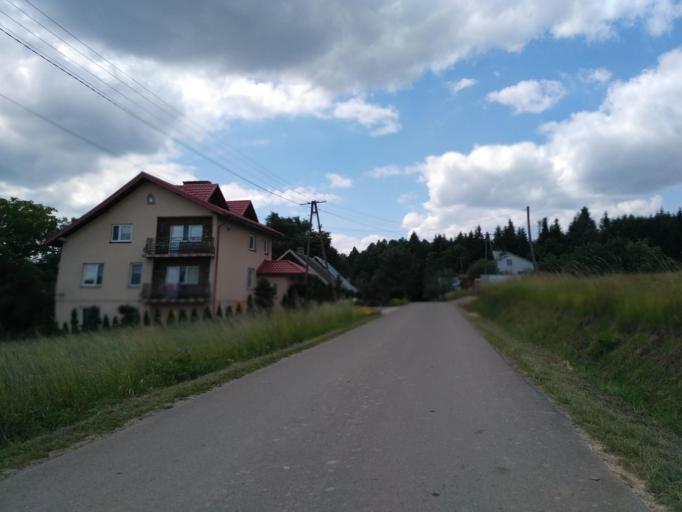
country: PL
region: Subcarpathian Voivodeship
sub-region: Powiat brzozowski
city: Wesola
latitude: 49.7590
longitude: 22.1320
